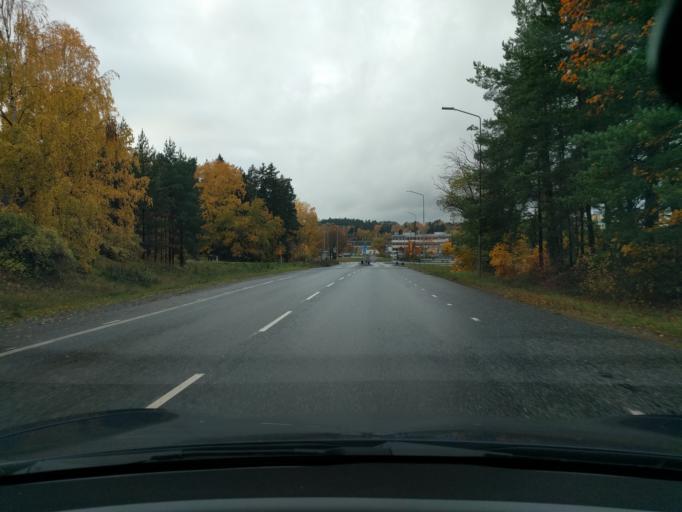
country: SE
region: Stockholm
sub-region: Taby Kommun
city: Taby
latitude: 59.4411
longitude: 18.0733
